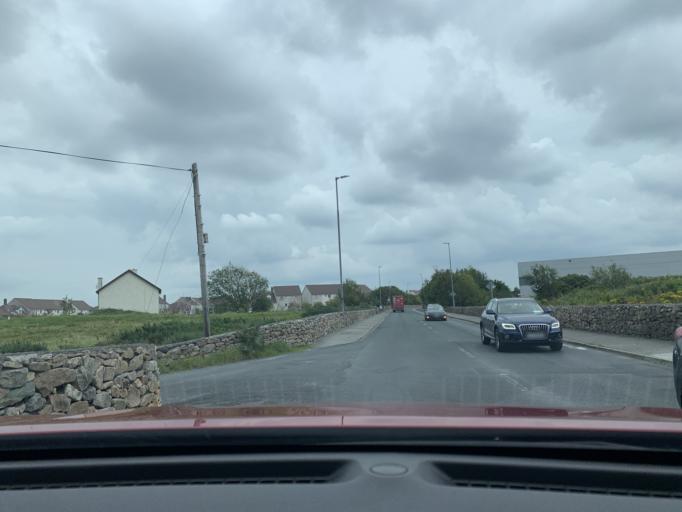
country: IE
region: Connaught
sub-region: County Galway
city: Gaillimh
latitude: 53.2770
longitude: -9.0956
